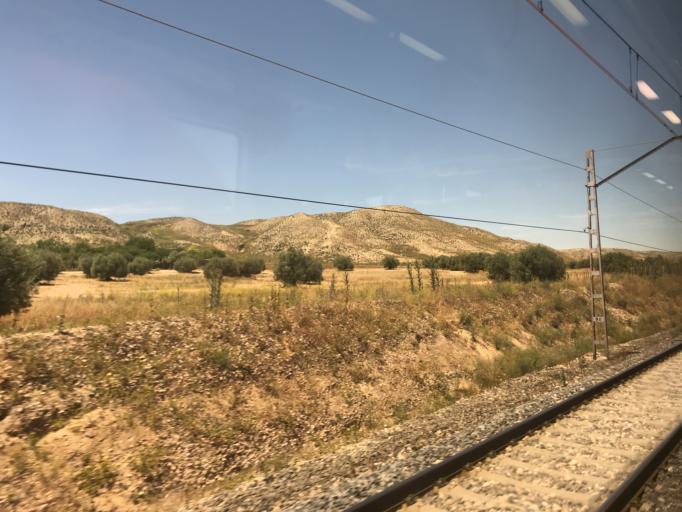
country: ES
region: Madrid
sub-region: Provincia de Madrid
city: Ciempozuelos
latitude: 40.1288
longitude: -3.6157
